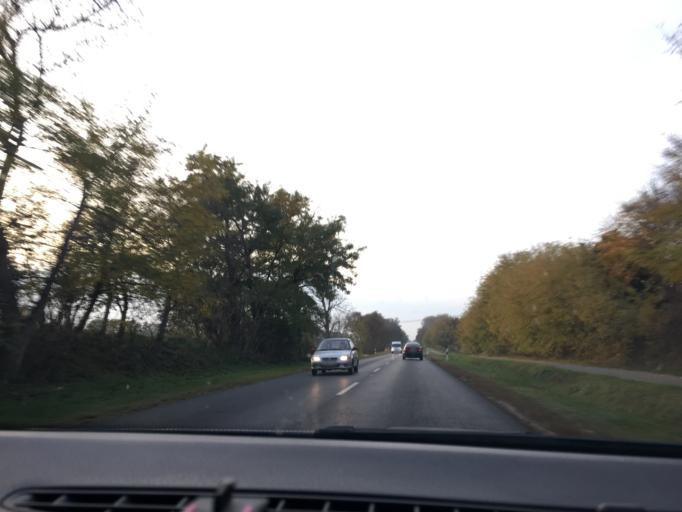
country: HU
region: Szabolcs-Szatmar-Bereg
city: Kallosemjen
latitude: 47.8611
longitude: 21.8931
